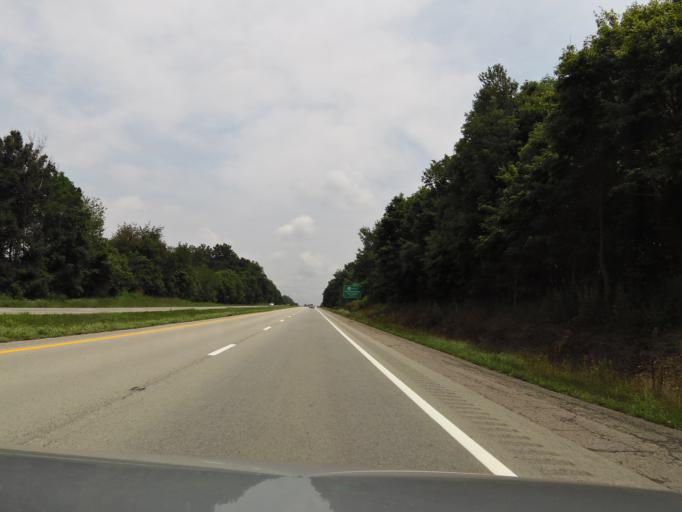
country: US
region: Kentucky
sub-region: Hardin County
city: Elizabethtown
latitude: 37.6371
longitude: -85.9271
